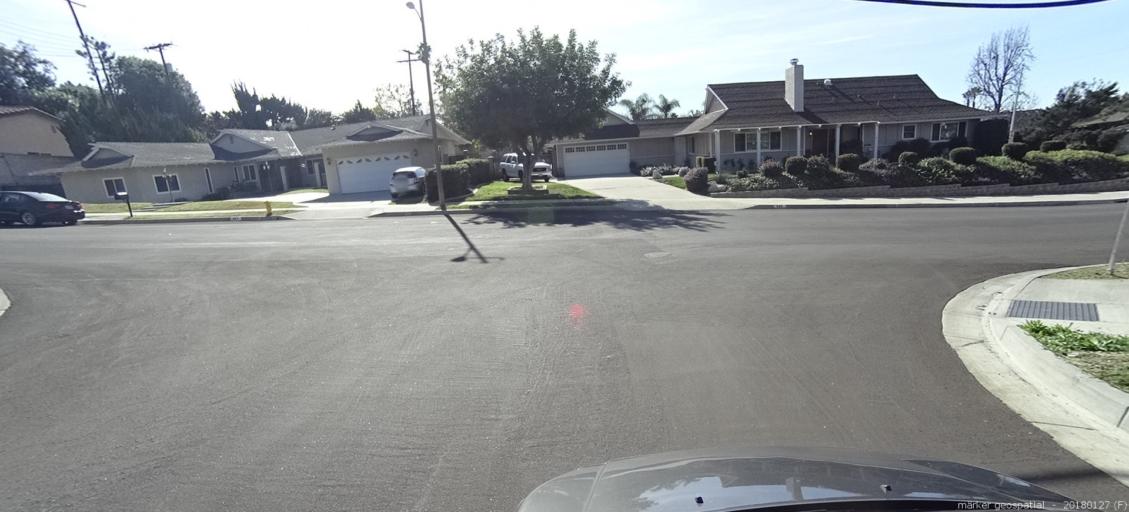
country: US
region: California
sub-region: Los Angeles County
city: Diamond Bar
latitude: 34.0201
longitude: -117.8050
